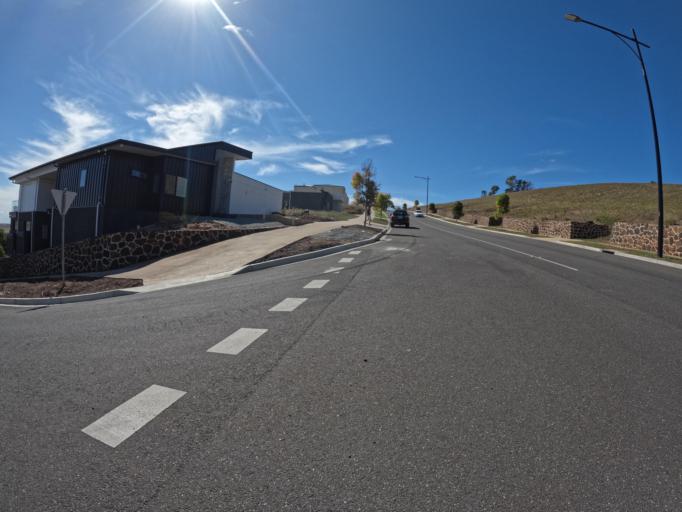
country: AU
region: Victoria
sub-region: Greater Geelong
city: Hamlyn Heights
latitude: -38.1313
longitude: 144.3151
